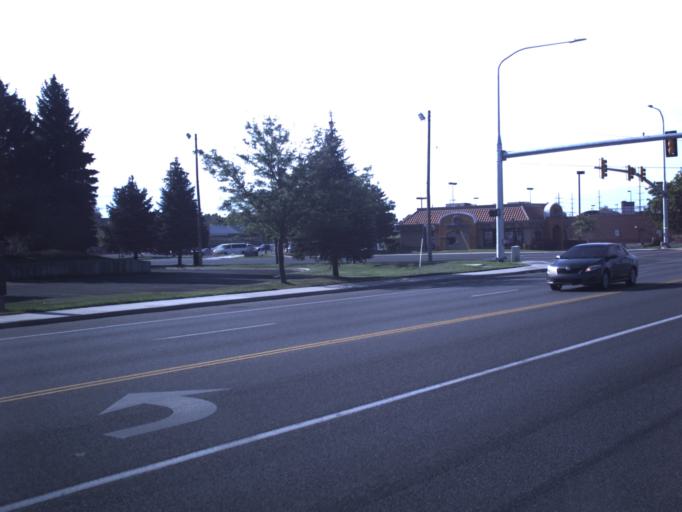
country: US
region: Utah
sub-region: Utah County
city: American Fork
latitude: 40.3650
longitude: -111.7856
